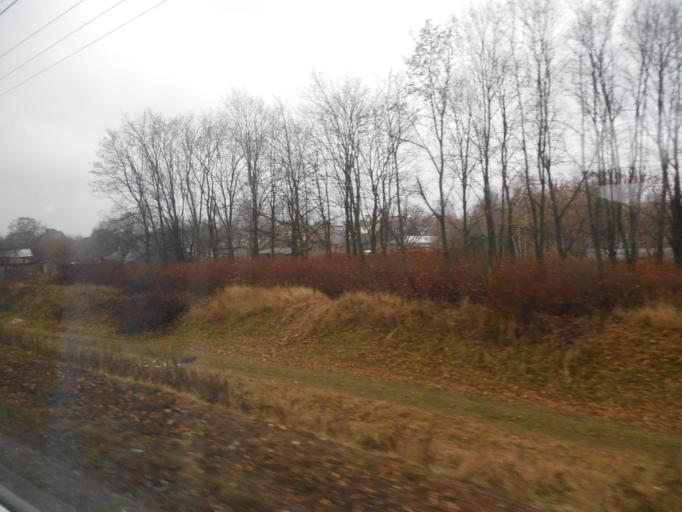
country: RU
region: Moskovskaya
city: Vidnoye
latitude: 55.5269
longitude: 37.7005
